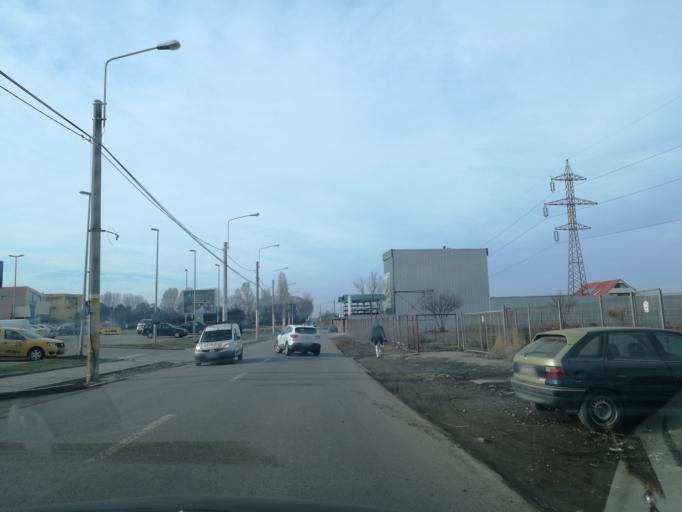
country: RO
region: Constanta
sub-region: Municipiul Constanta
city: Constanta
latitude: 44.1890
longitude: 28.6107
